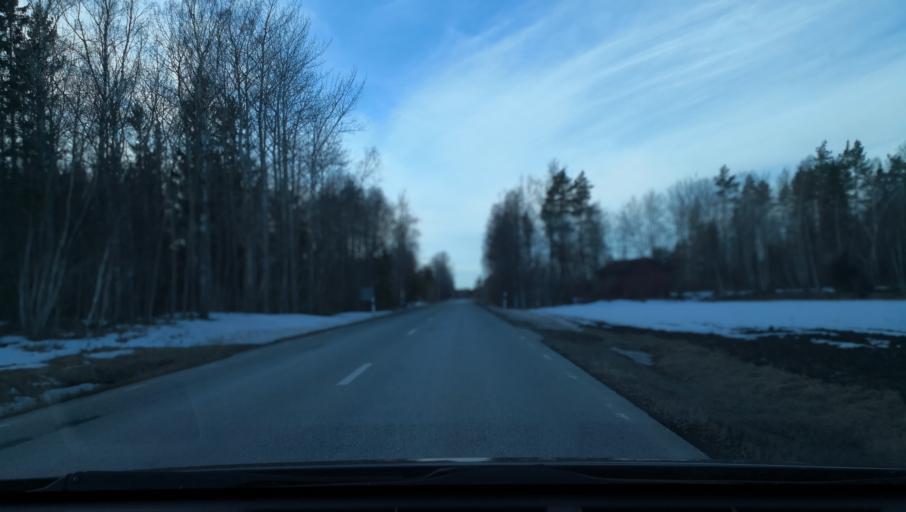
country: SE
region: Uppsala
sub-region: Osthammars Kommun
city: OEsthammar
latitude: 60.3240
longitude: 18.2510
